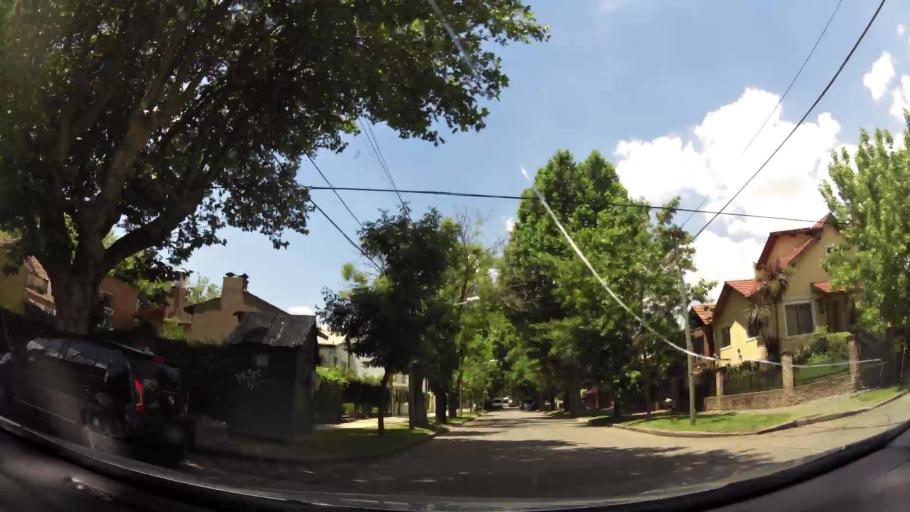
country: AR
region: Buenos Aires
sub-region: Partido de Tigre
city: Tigre
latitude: -34.4183
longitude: -58.5827
